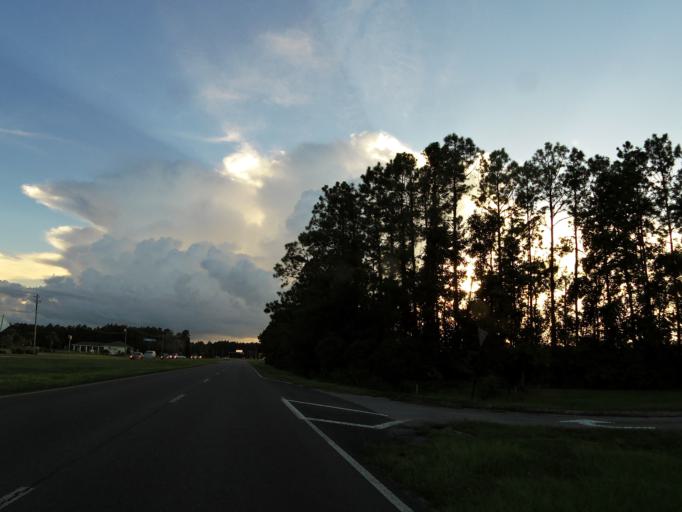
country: US
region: Georgia
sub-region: Camden County
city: St Marys
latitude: 30.7817
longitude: -81.6176
